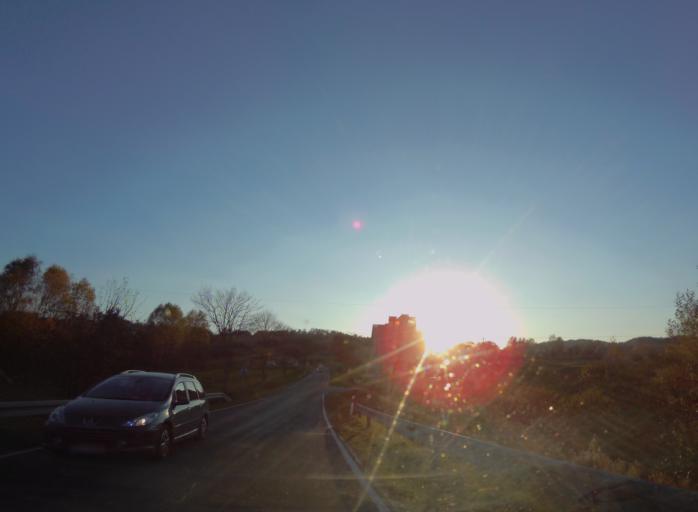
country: PL
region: Subcarpathian Voivodeship
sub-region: Powiat leski
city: Polanczyk
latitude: 49.3780
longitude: 22.4197
